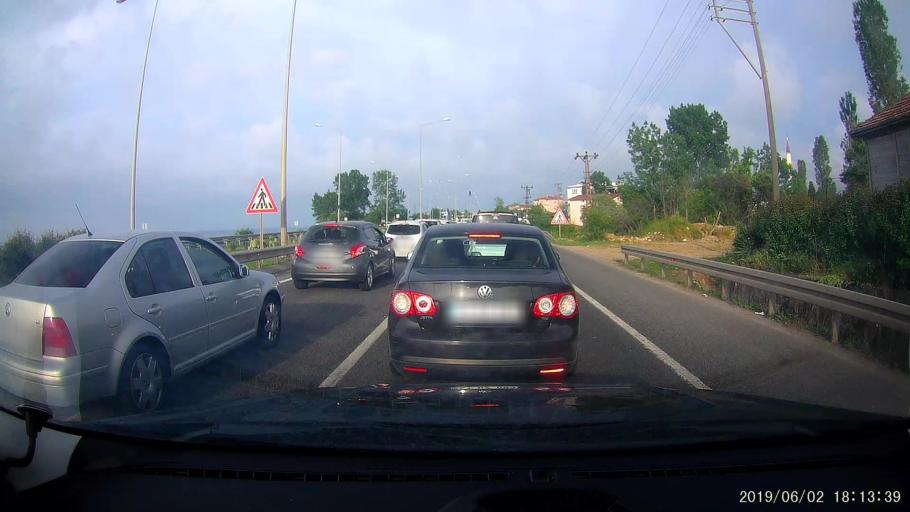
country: TR
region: Ordu
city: Unieh
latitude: 41.1066
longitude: 37.3682
